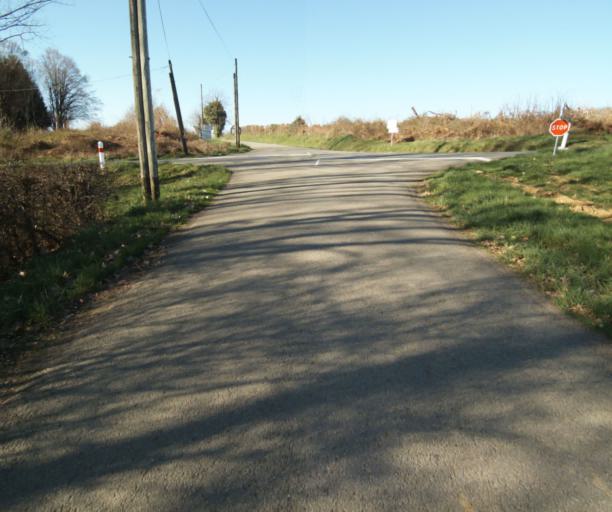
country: FR
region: Limousin
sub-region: Departement de la Correze
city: Seilhac
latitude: 45.3870
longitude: 1.7573
